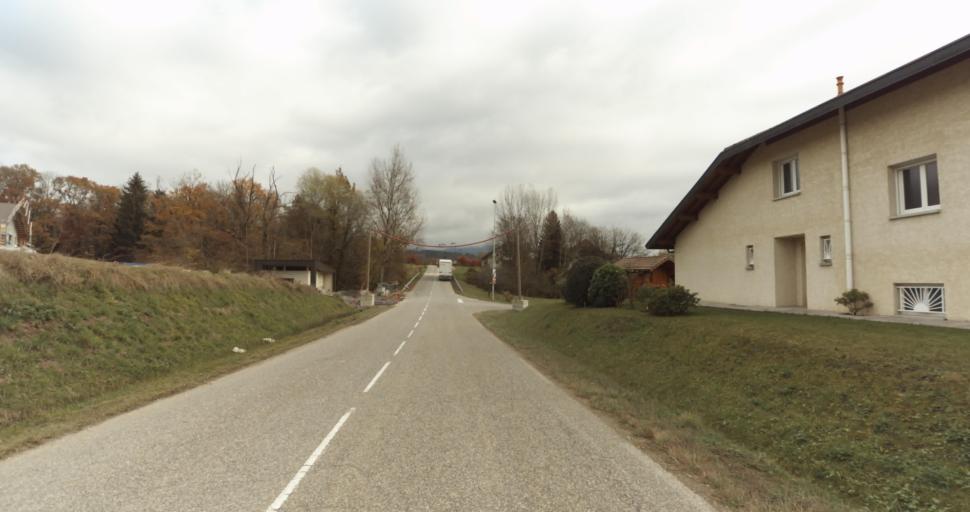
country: FR
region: Rhone-Alpes
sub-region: Departement de la Haute-Savoie
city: Pringy
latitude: 45.9555
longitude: 6.1096
